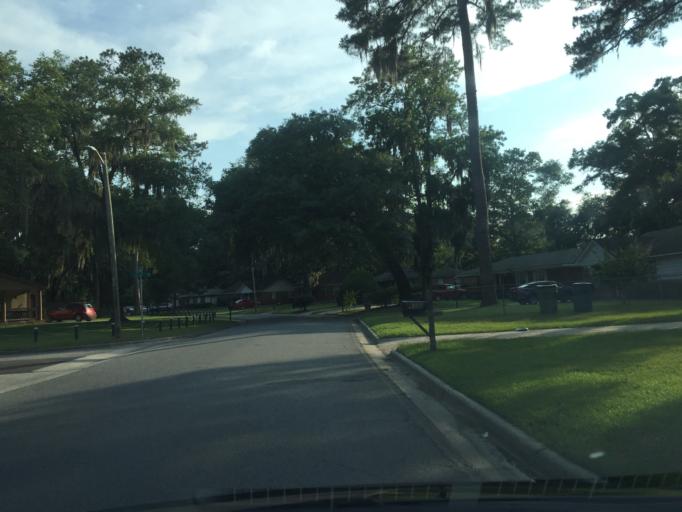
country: US
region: Georgia
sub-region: Chatham County
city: Montgomery
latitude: 31.9918
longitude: -81.1204
